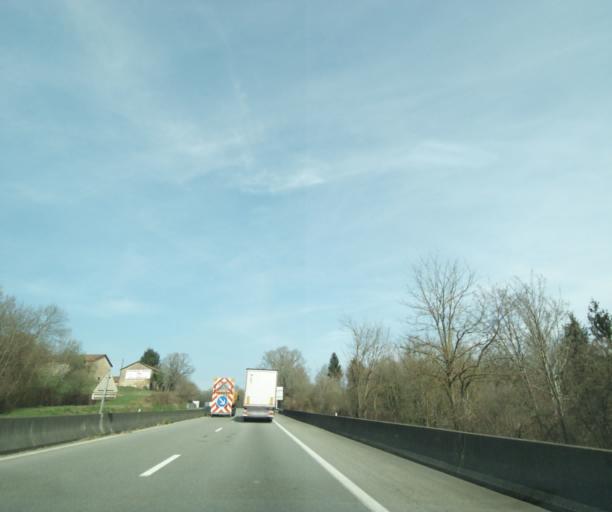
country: FR
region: Limousin
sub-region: Departement de la Haute-Vienne
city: Boisseuil
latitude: 45.7442
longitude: 1.3405
